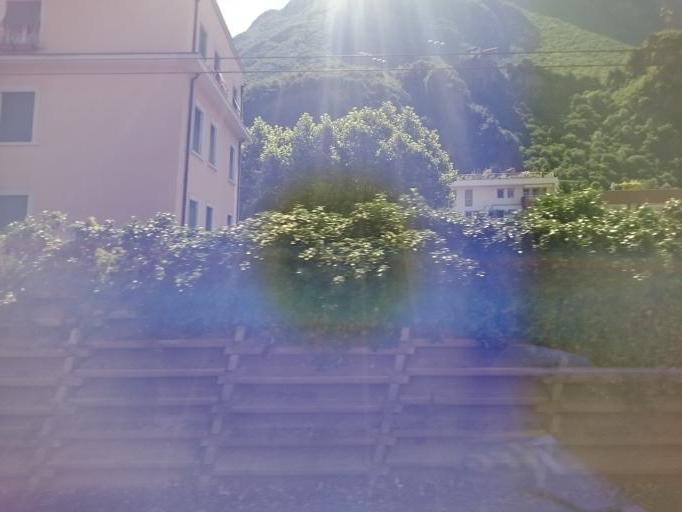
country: IT
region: Trentino-Alto Adige
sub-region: Bolzano
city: Bolzano
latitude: 46.4790
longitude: 11.3387
